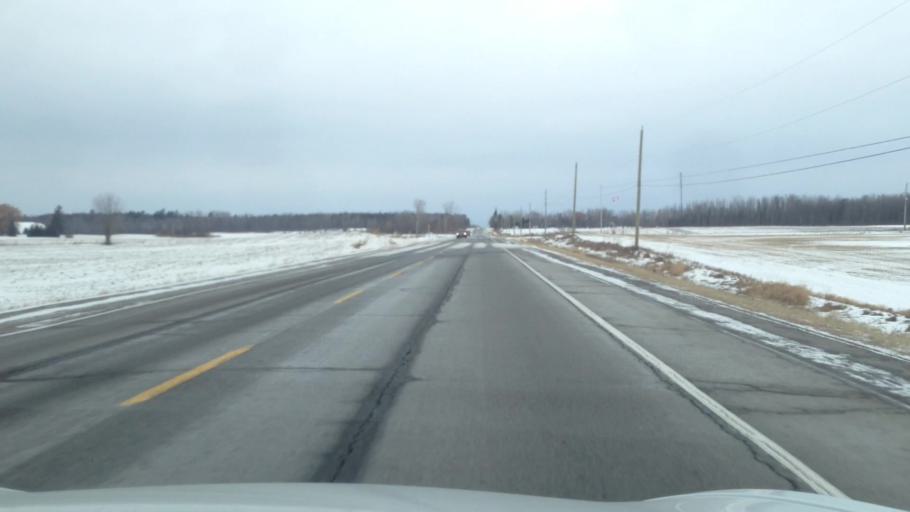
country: CA
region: Ontario
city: Clarence-Rockland
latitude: 45.4059
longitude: -75.3993
